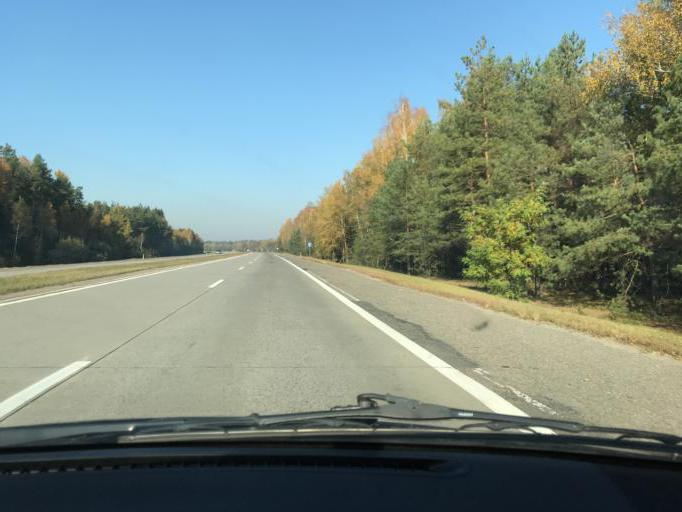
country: BY
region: Minsk
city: Uzda
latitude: 53.3650
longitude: 27.5093
